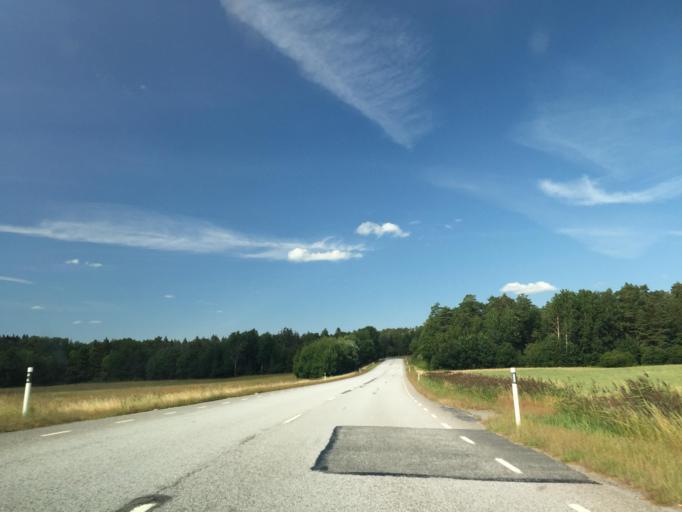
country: SE
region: Vaestra Goetaland
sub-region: Tanums Kommun
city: Tanumshede
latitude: 58.8141
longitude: 11.2628
